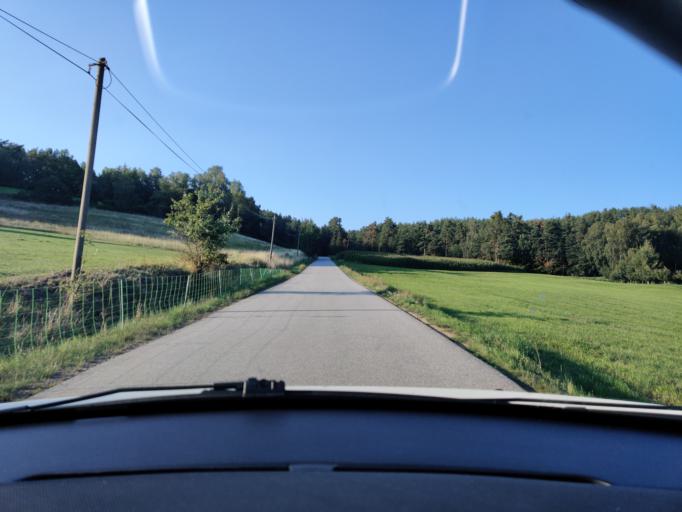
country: DE
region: Bavaria
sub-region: Upper Palatinate
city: Nabburg
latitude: 49.4136
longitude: 12.1767
